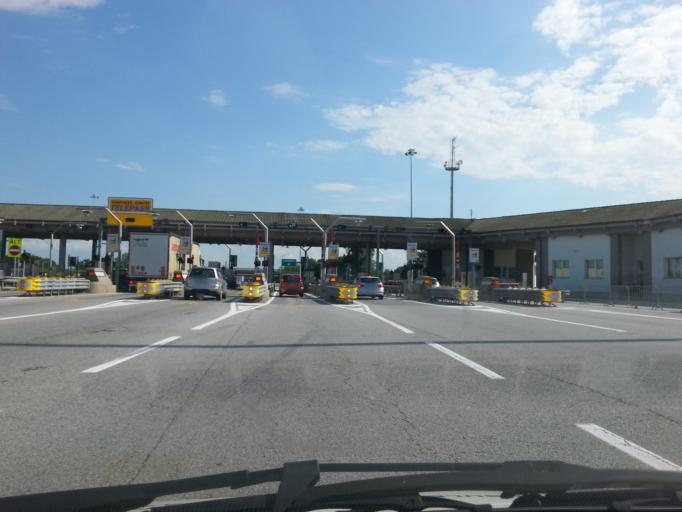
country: IT
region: Piedmont
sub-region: Provincia di Torino
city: Carmagnola
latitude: 44.8548
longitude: 7.7482
